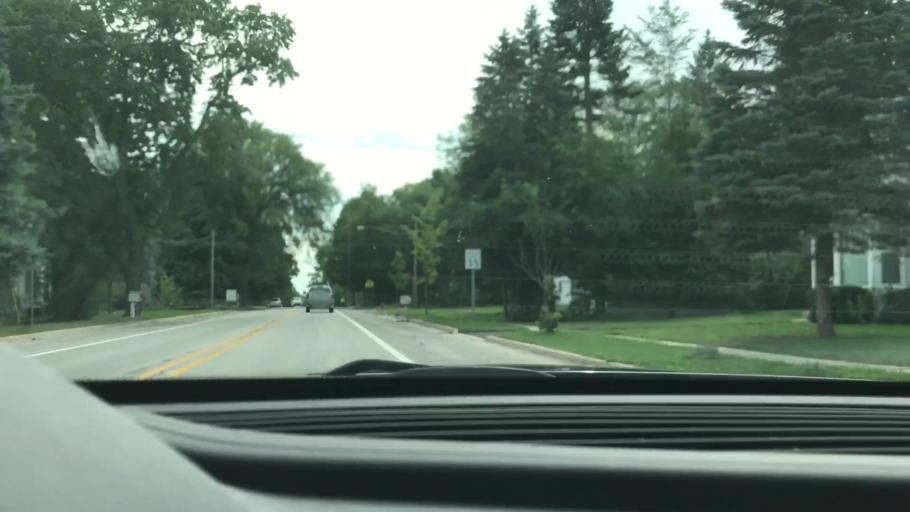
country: US
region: Michigan
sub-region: Antrim County
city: Bellaire
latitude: 44.9835
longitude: -85.2103
